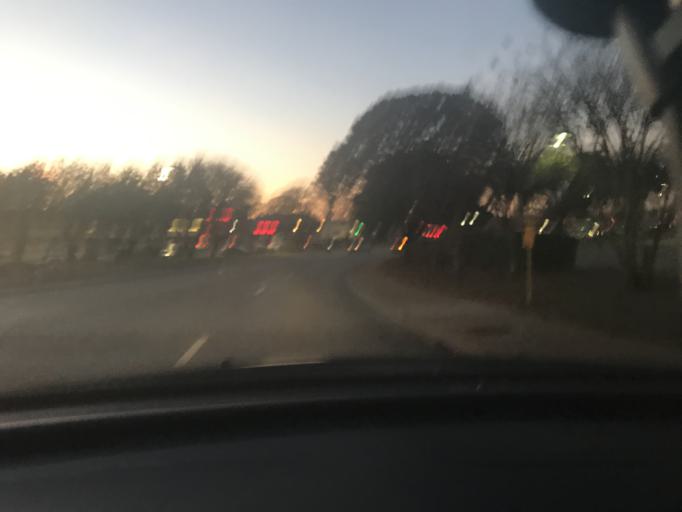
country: US
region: Texas
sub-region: Tarrant County
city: Arlington
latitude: 32.7557
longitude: -97.0998
